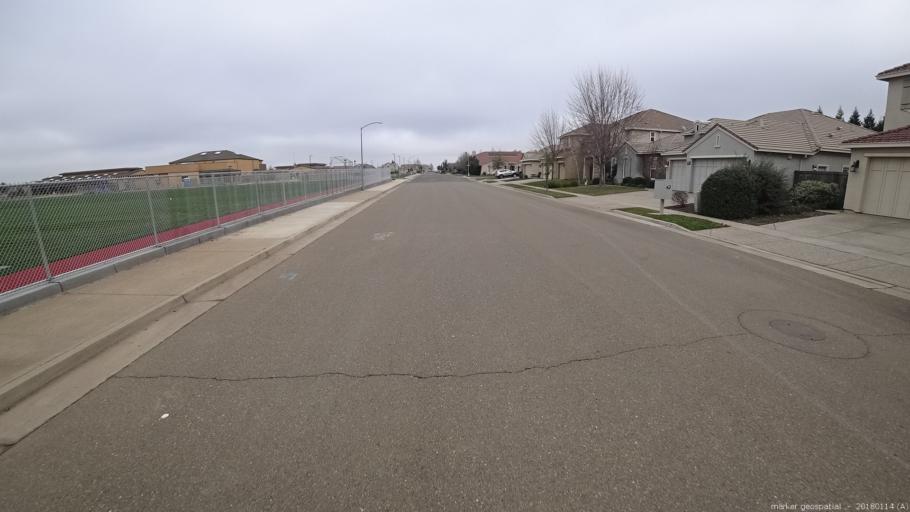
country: US
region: California
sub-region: Sacramento County
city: Rancho Cordova
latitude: 38.5435
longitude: -121.2323
